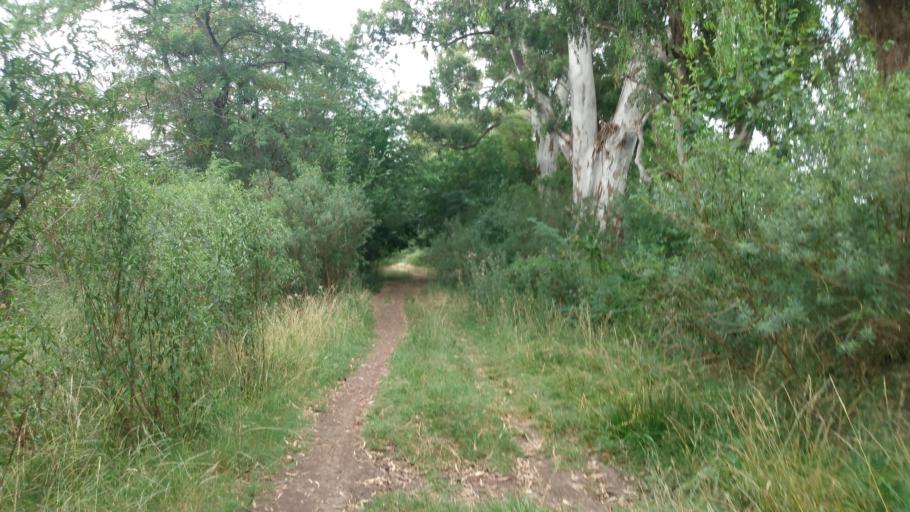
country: AR
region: Buenos Aires
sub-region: Partido de Lujan
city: Lujan
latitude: -34.6015
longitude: -59.0653
